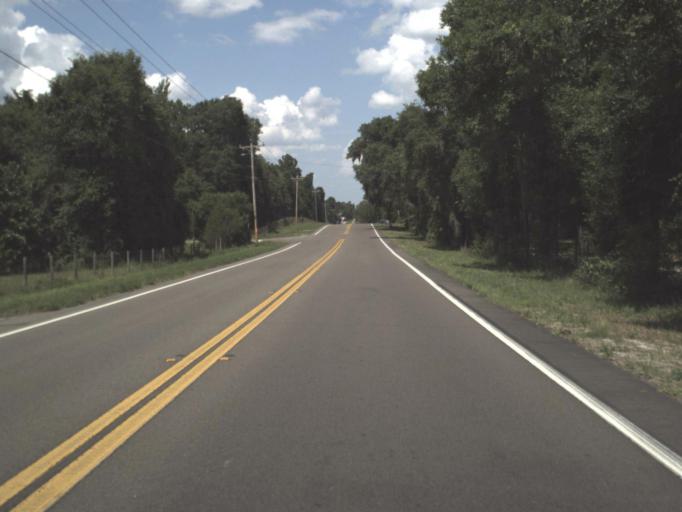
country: US
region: Florida
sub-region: Clay County
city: Keystone Heights
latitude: 29.7243
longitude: -81.9903
